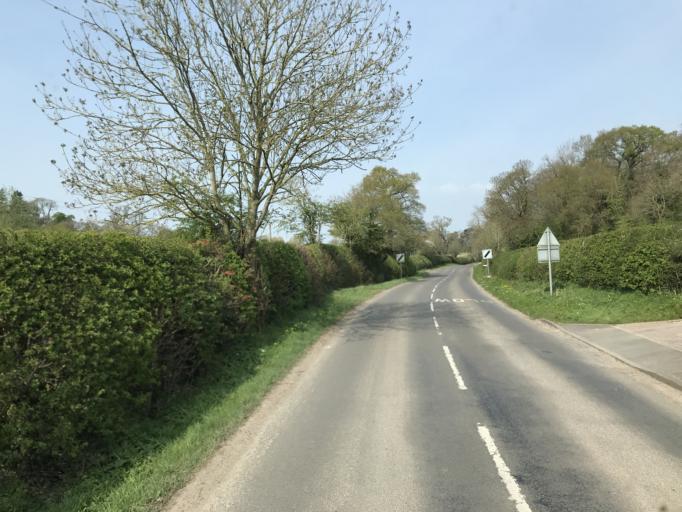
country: GB
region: England
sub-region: Cheshire West and Chester
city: Aldford
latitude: 53.1302
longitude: -2.8652
